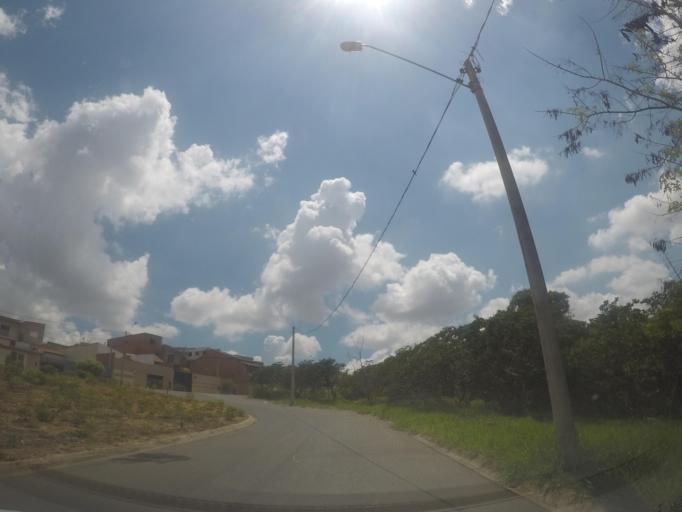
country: BR
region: Sao Paulo
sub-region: Hortolandia
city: Hortolandia
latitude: -22.8407
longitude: -47.1994
